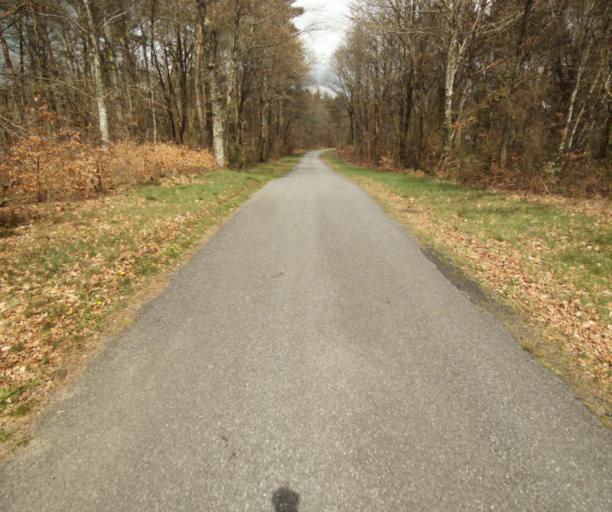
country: FR
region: Limousin
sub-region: Departement de la Correze
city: Correze
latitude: 45.3228
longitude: 1.8946
